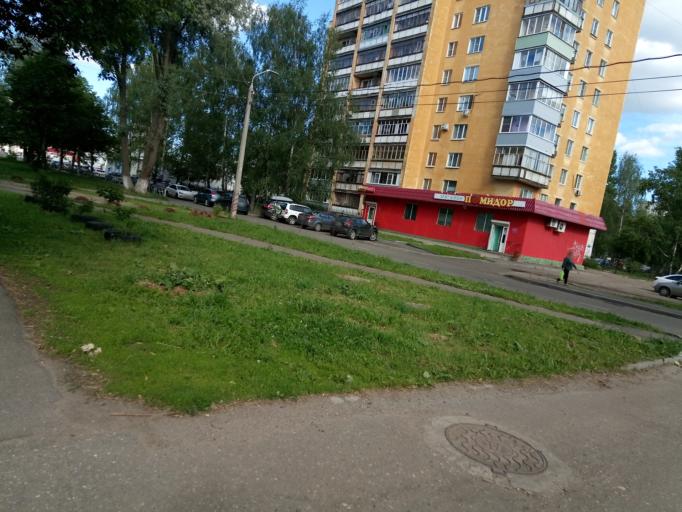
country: RU
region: Jaroslavl
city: Yaroslavl
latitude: 57.6503
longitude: 39.9446
